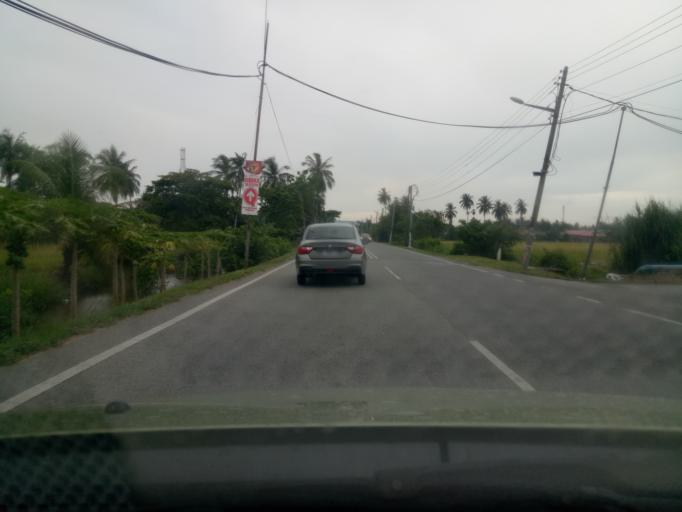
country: MY
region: Kedah
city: Alor Setar
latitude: 5.9739
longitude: 100.4059
